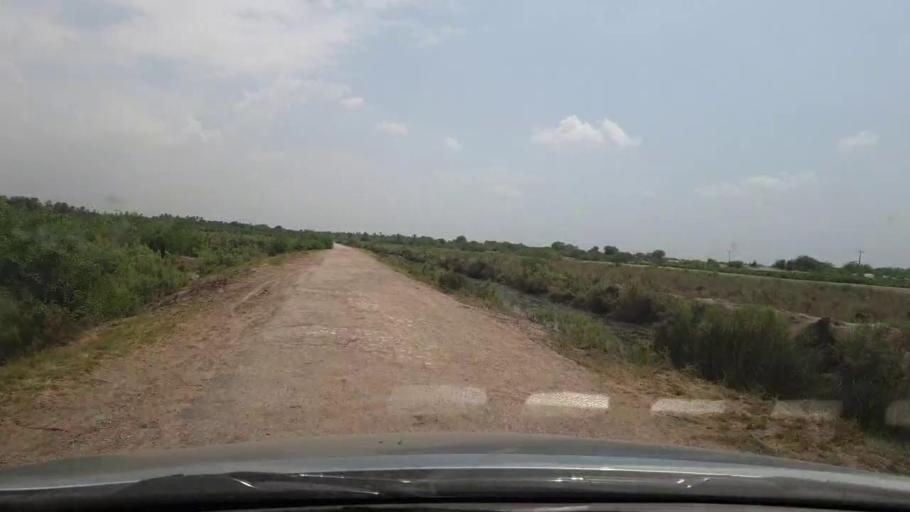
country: PK
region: Sindh
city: Kot Diji
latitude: 27.3871
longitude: 68.7149
